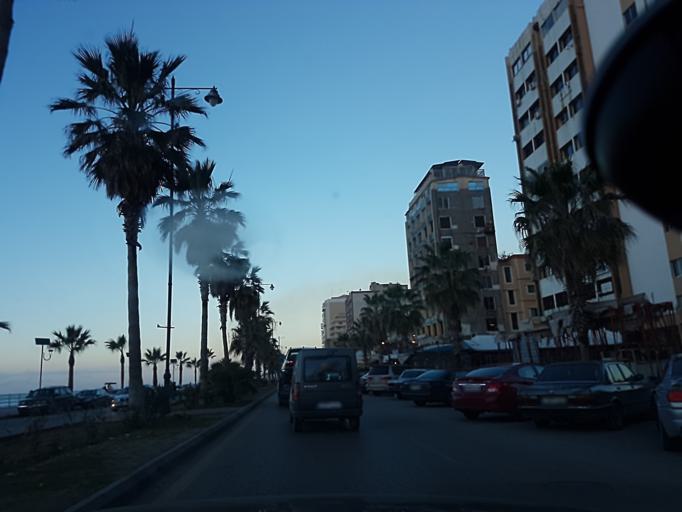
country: LB
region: Liban-Sud
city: Sidon
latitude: 33.5681
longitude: 35.3762
